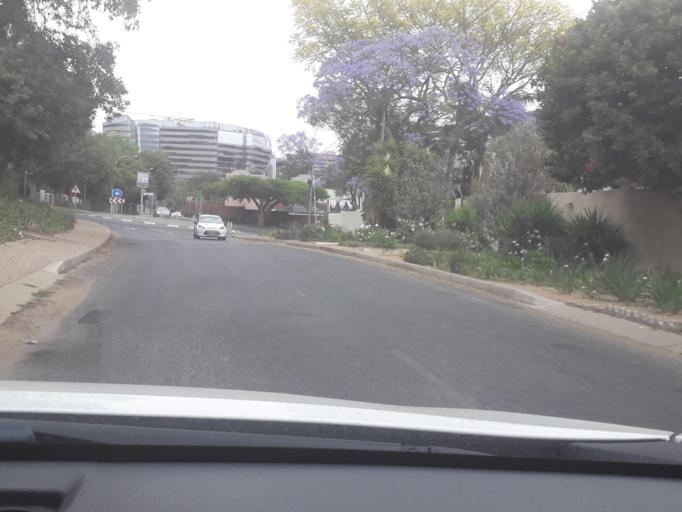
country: ZA
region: Gauteng
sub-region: City of Johannesburg Metropolitan Municipality
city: Johannesburg
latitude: -26.1098
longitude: 28.0618
